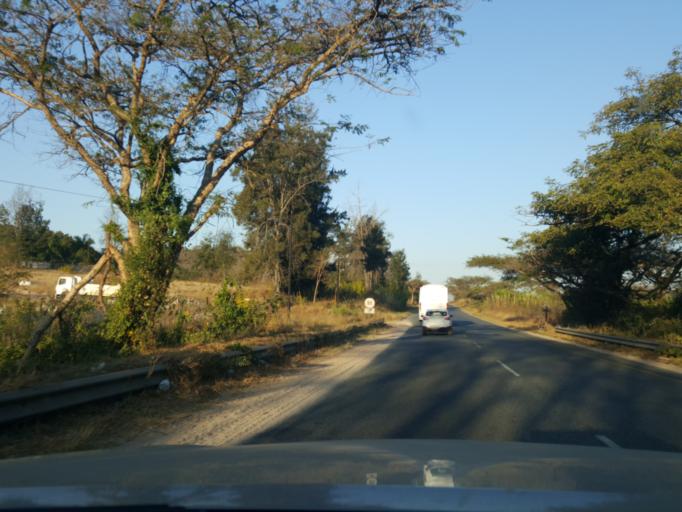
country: ZA
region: Mpumalanga
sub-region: Ehlanzeni District
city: Nelspruit
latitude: -25.4650
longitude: 31.0839
